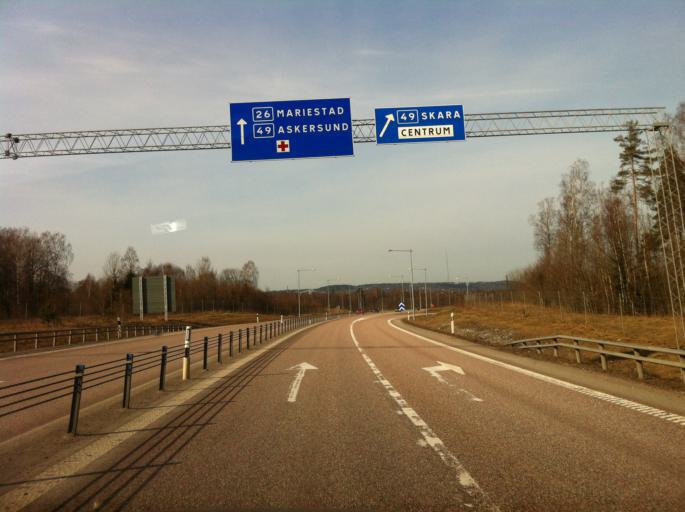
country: SE
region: Vaestra Goetaland
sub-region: Skovde Kommun
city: Skultorp
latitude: 58.3644
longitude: 13.8585
